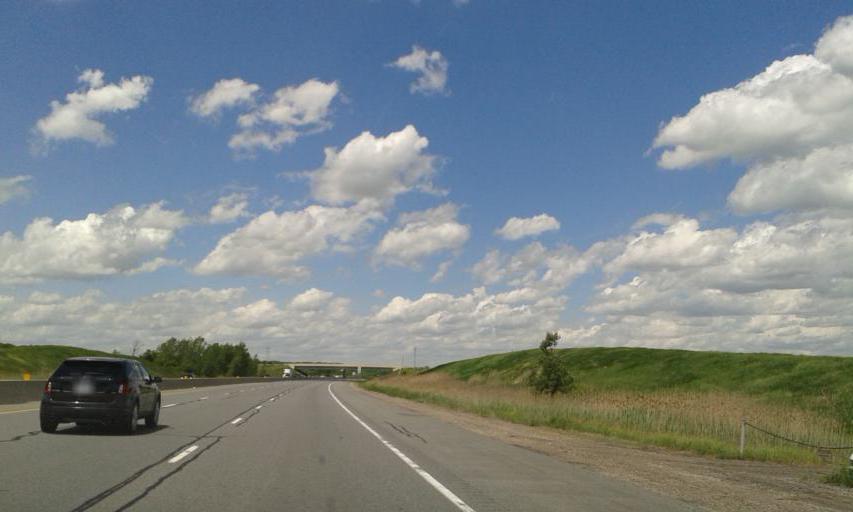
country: CA
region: Ontario
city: Burlington
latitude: 43.3942
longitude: -79.8340
